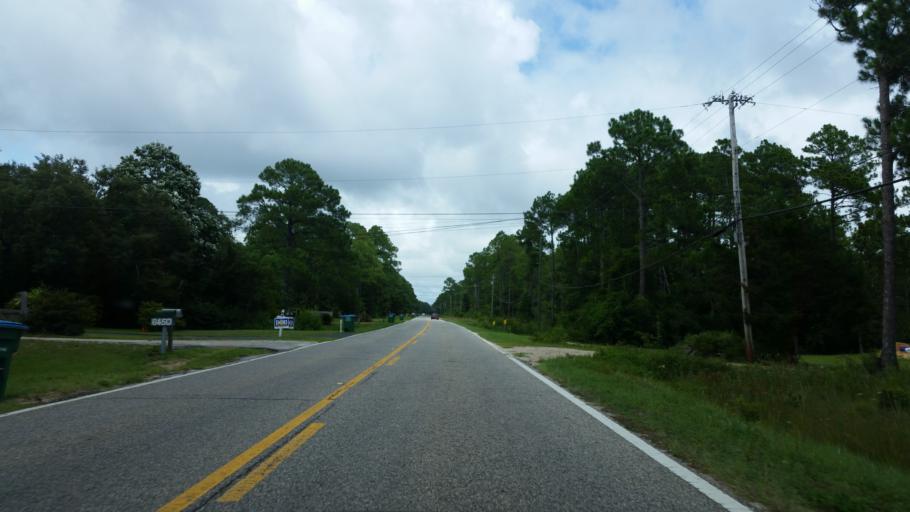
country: US
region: Florida
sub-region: Santa Rosa County
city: Holley
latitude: 30.4345
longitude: -86.9594
